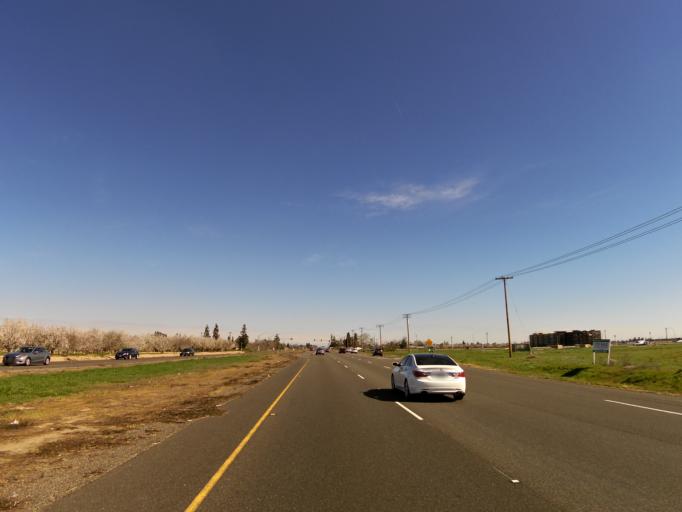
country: US
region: California
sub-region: Stanislaus County
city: Salida
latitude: 37.7113
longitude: -121.0538
